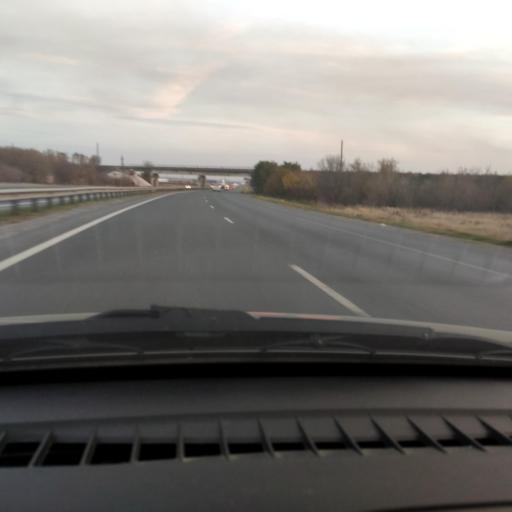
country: RU
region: Samara
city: Tol'yatti
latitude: 53.5644
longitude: 49.4956
